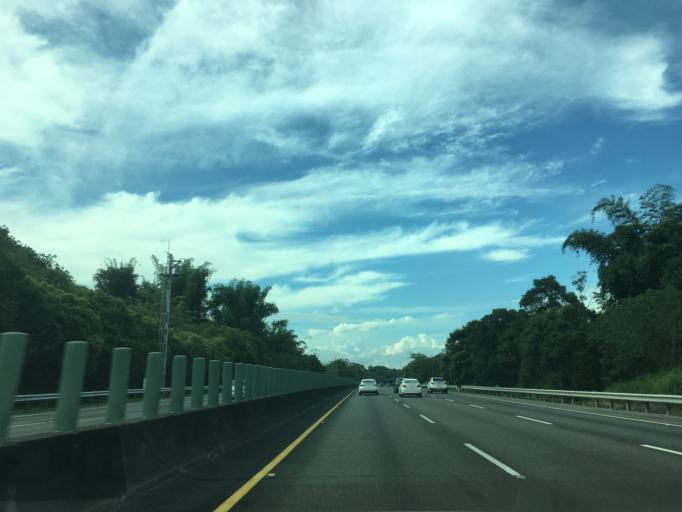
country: TW
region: Taiwan
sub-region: Chiayi
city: Jiayi Shi
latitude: 23.5634
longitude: 120.5050
